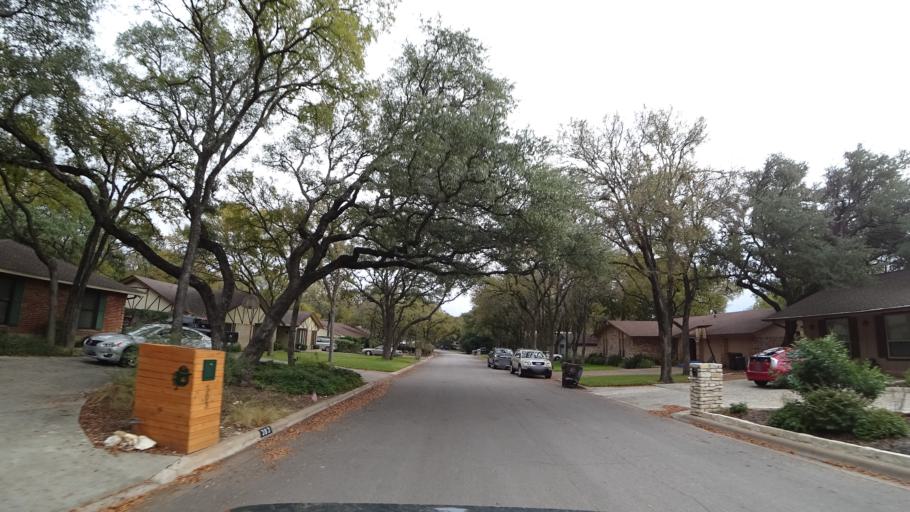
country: US
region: Texas
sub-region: Williamson County
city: Round Rock
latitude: 30.5038
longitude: -97.6981
